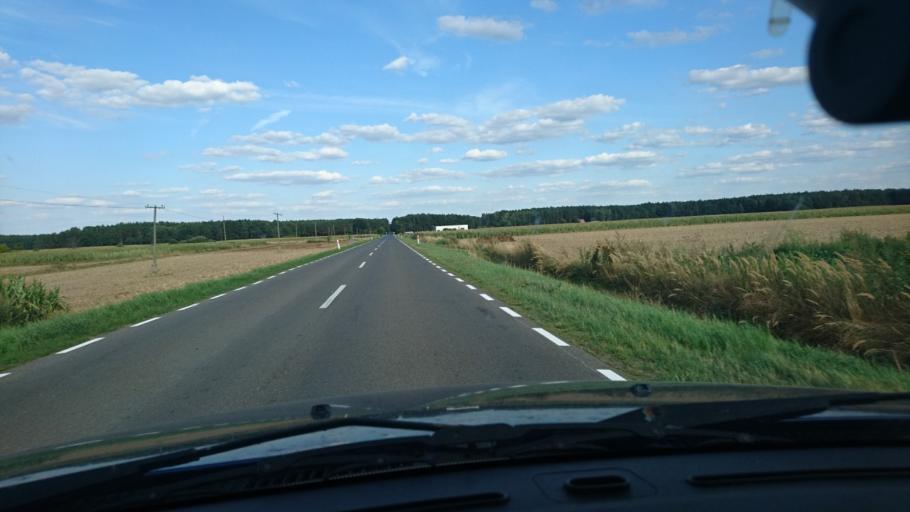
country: PL
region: Greater Poland Voivodeship
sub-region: Powiat krotoszynski
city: Sulmierzyce
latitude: 51.6048
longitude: 17.5626
